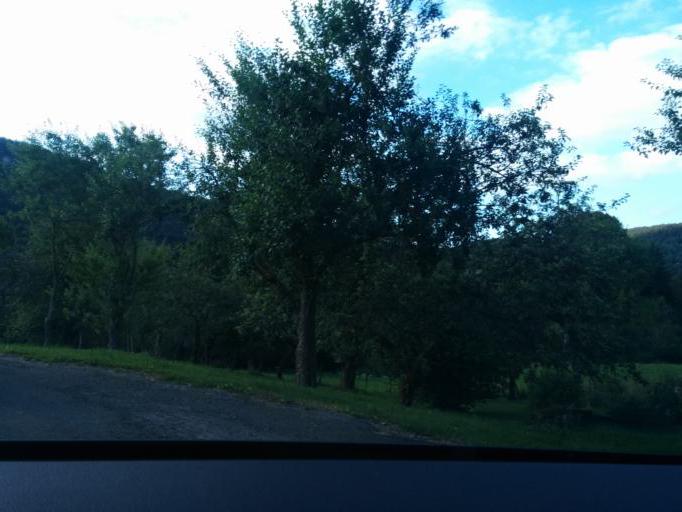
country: FR
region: Franche-Comte
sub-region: Departement du Jura
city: Valfin-les-Saint-Claude
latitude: 46.4437
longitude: 5.8288
